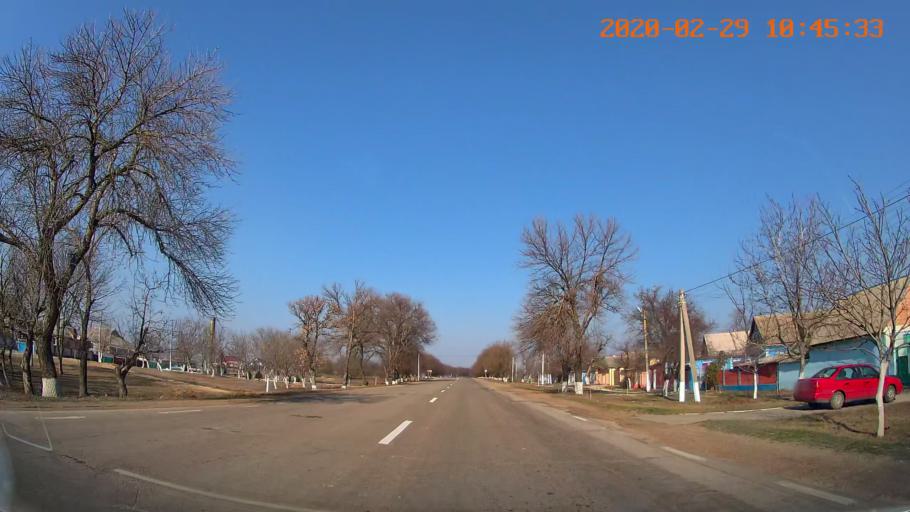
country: MD
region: Telenesti
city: Grigoriopol
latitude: 47.0767
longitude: 29.3820
